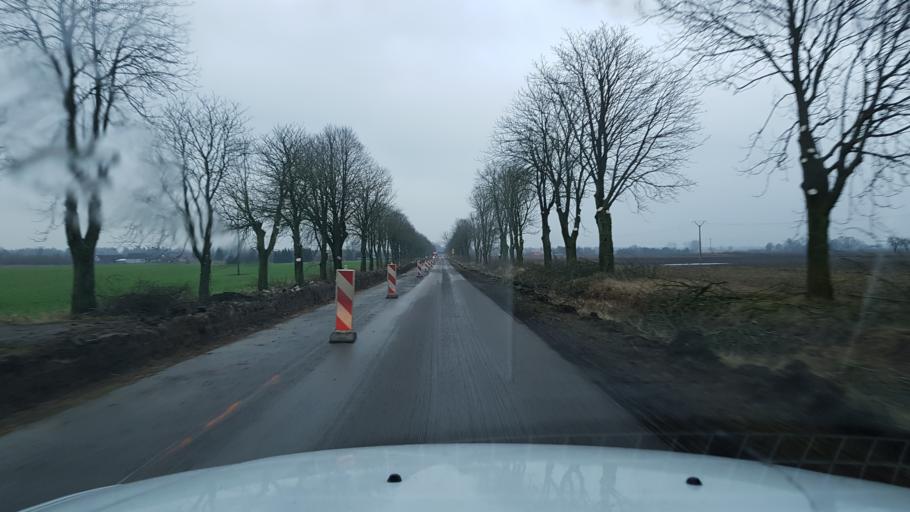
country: PL
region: West Pomeranian Voivodeship
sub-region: Powiat gryficki
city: Ploty
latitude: 53.8267
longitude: 15.2478
